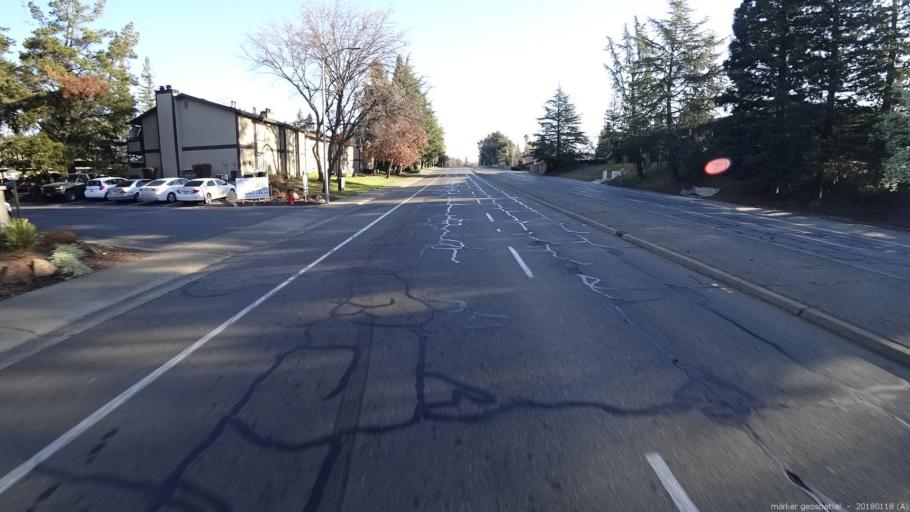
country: US
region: California
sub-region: Sacramento County
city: Orangevale
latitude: 38.6672
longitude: -121.2113
